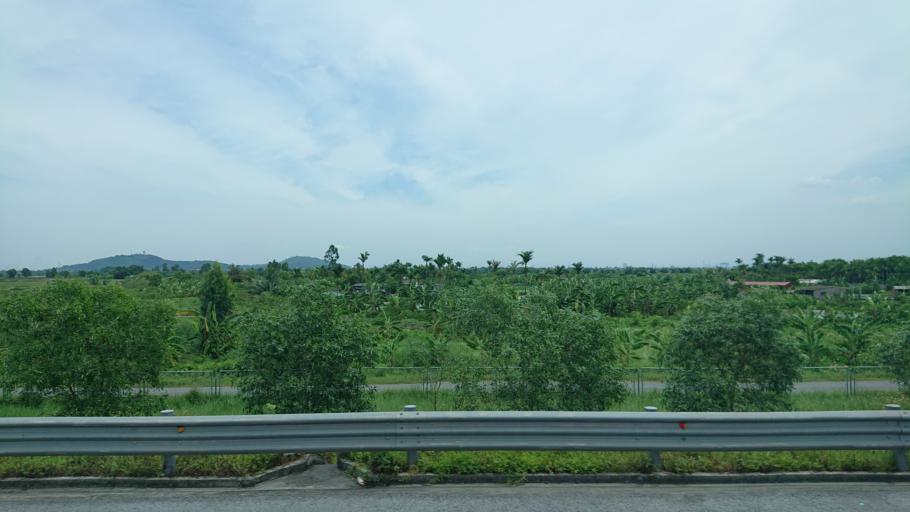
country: VN
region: Hai Phong
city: Nui Doi
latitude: 20.7669
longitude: 106.6422
